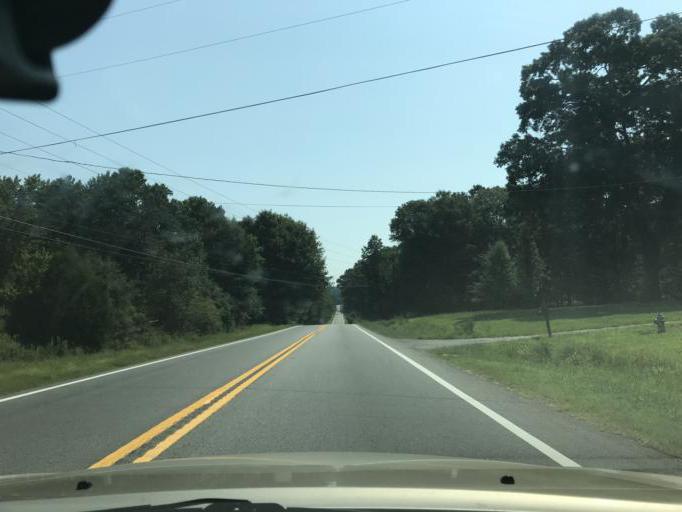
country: US
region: Georgia
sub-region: Hall County
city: Flowery Branch
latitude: 34.2480
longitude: -84.0162
